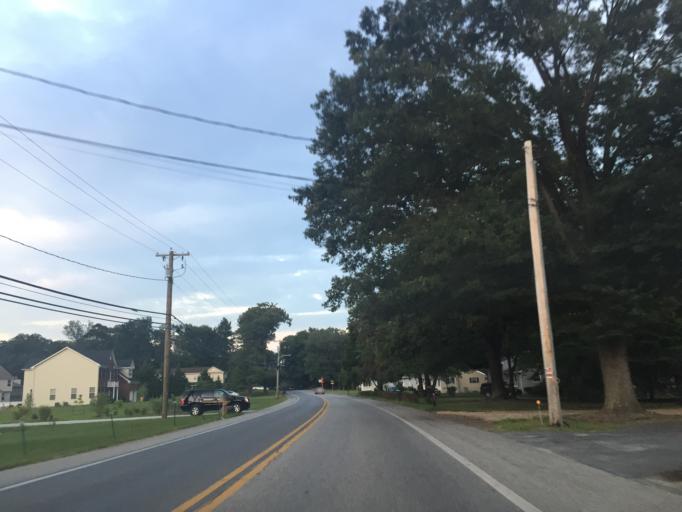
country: US
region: Maryland
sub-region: Anne Arundel County
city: Gambrills
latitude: 39.0720
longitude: -76.6771
